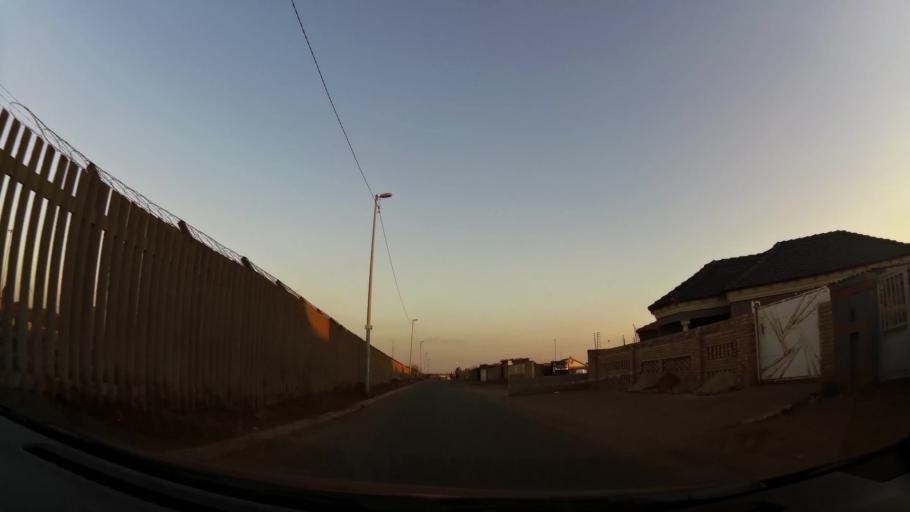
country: ZA
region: Gauteng
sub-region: City of Johannesburg Metropolitan Municipality
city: Soweto
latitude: -26.2286
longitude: 27.8434
